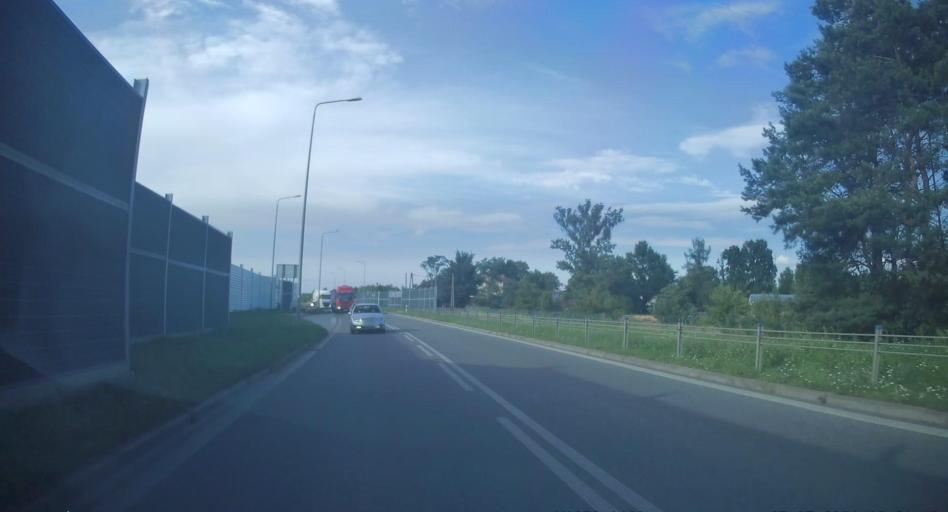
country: PL
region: Swietokrzyskie
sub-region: Powiat konecki
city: Konskie
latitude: 51.1280
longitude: 20.3596
